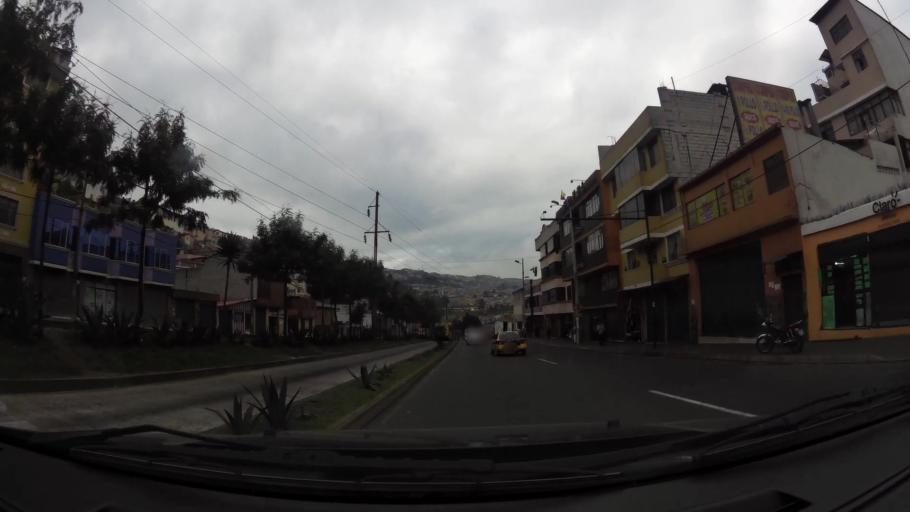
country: EC
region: Pichincha
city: Quito
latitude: -0.2259
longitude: -78.5067
